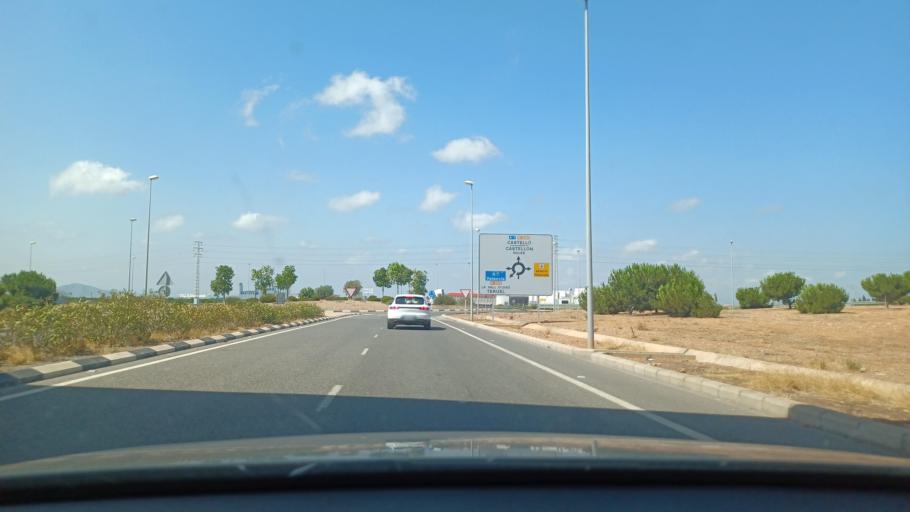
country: ES
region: Valencia
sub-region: Provincia de Castello
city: Moncofar
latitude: 39.8158
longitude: -0.1669
